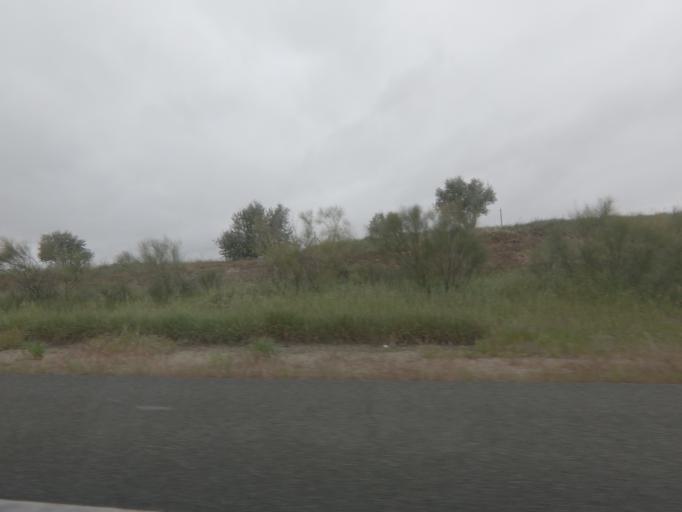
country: ES
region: Extremadura
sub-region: Provincia de Caceres
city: Casar de Caceres
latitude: 39.5397
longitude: -6.4057
